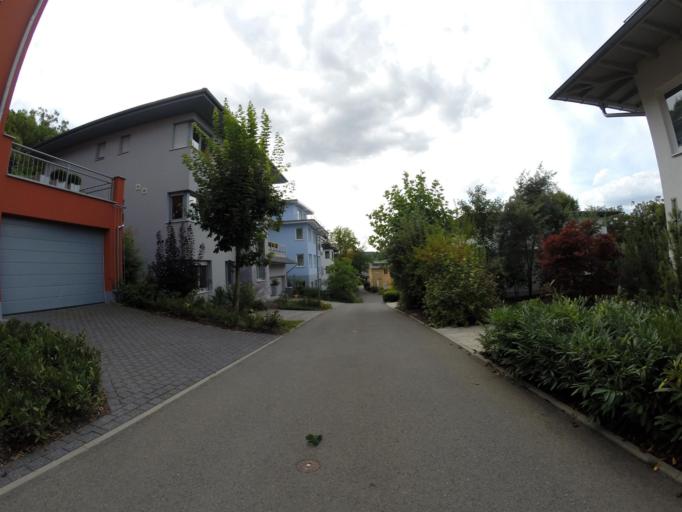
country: DE
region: Thuringia
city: Jena
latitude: 50.9158
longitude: 11.5940
